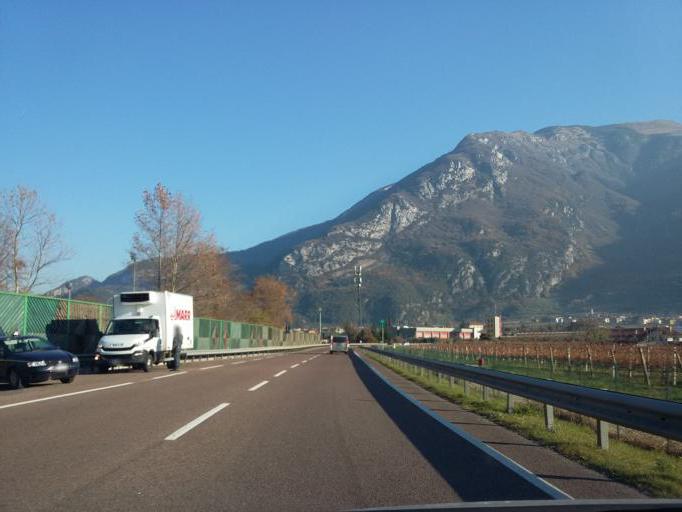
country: IT
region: Trentino-Alto Adige
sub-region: Provincia di Trento
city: Arco
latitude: 45.9127
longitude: 10.8862
